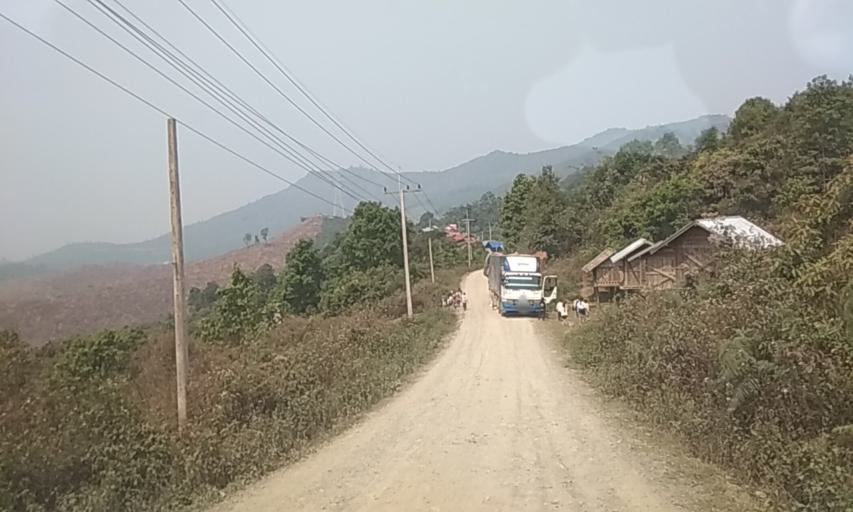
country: TH
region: Nan
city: Chaloem Phra Kiat
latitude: 20.0175
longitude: 101.1071
